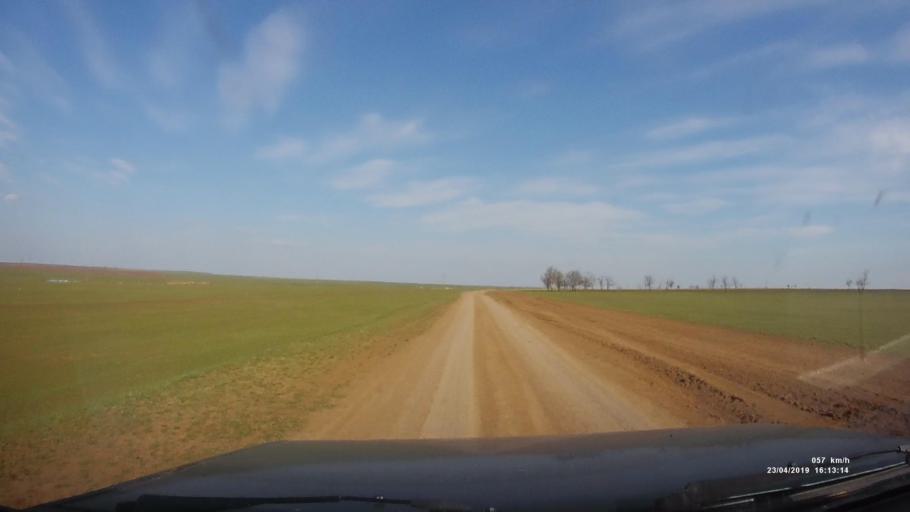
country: RU
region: Kalmykiya
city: Priyutnoye
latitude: 46.4645
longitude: 43.1325
